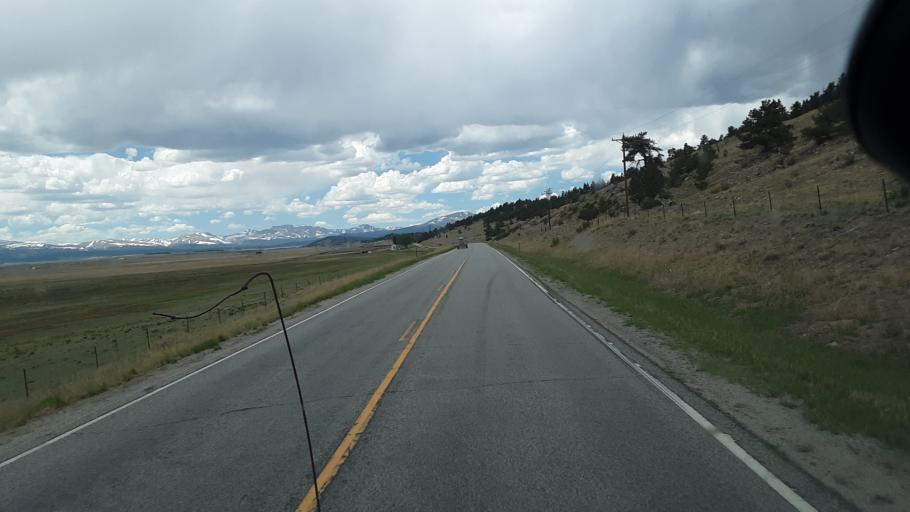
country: US
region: Colorado
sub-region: Park County
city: Fairplay
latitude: 39.0659
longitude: -105.8566
